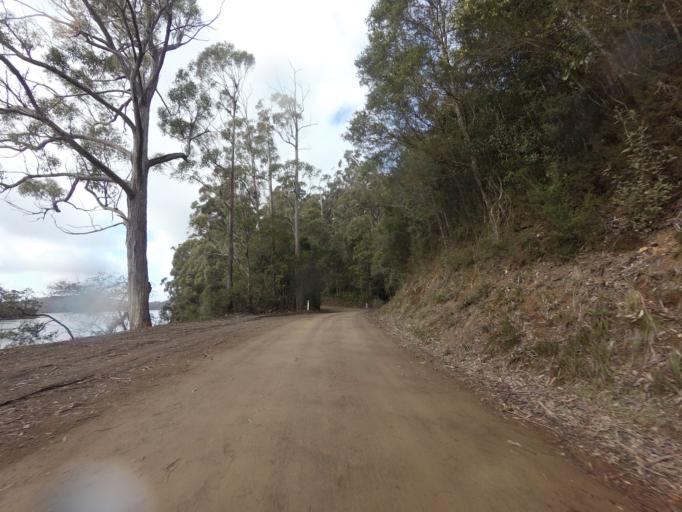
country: AU
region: Tasmania
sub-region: Huon Valley
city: Geeveston
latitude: -43.5668
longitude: 146.8871
